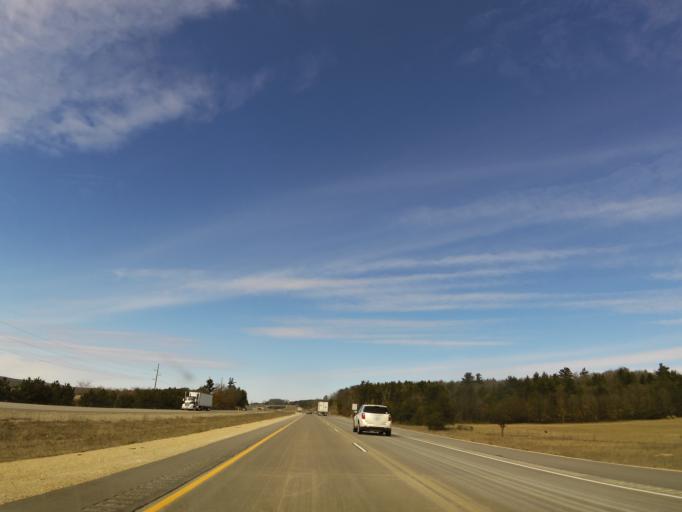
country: US
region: Wisconsin
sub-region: Monroe County
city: Tomah
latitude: 44.0766
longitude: -90.5236
